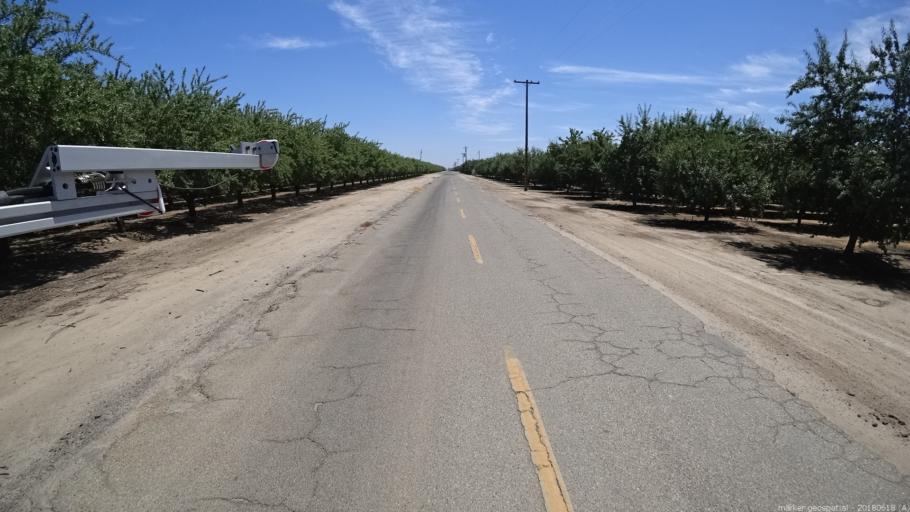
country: US
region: California
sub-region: Madera County
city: Madera
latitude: 36.9093
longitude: -120.1348
